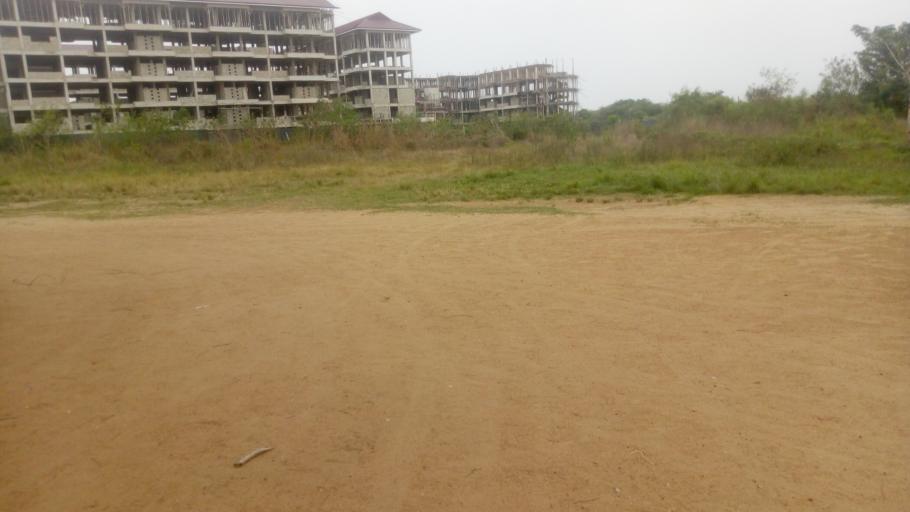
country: GH
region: Central
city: Winneba
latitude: 5.3667
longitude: -0.6313
